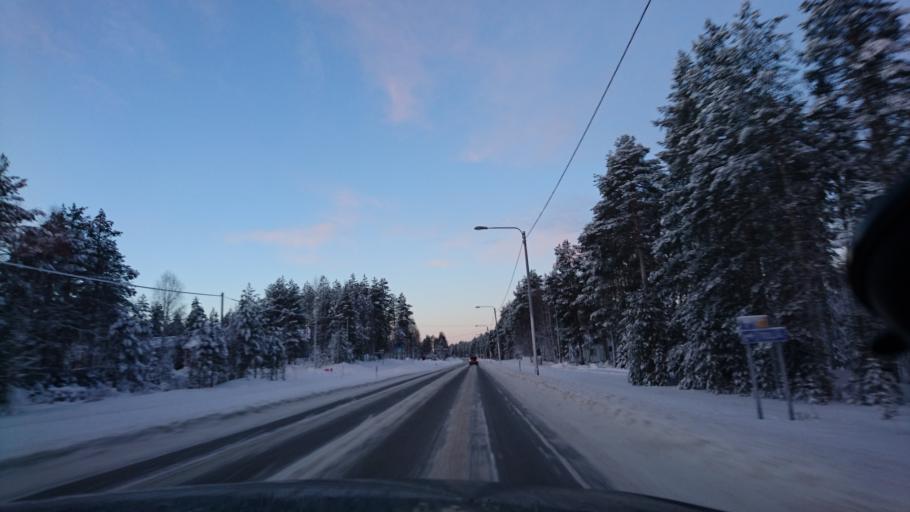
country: FI
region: Lapland
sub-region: Rovaniemi
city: Ranua
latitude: 65.9414
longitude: 26.4776
